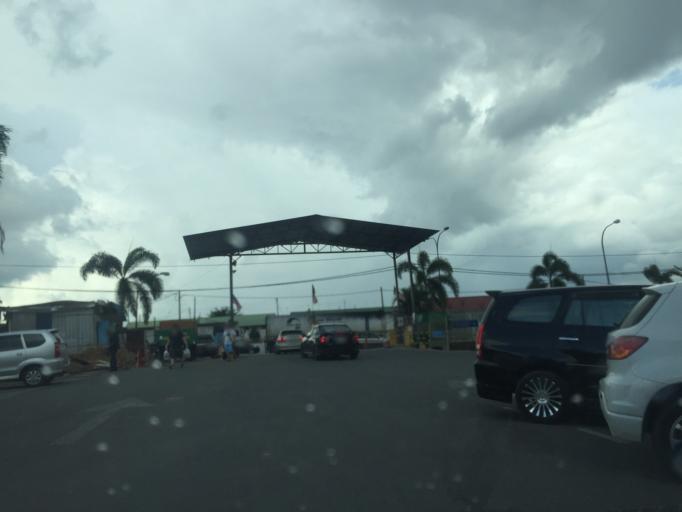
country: TH
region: Songkhla
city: Sadao
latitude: 6.5170
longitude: 100.4189
